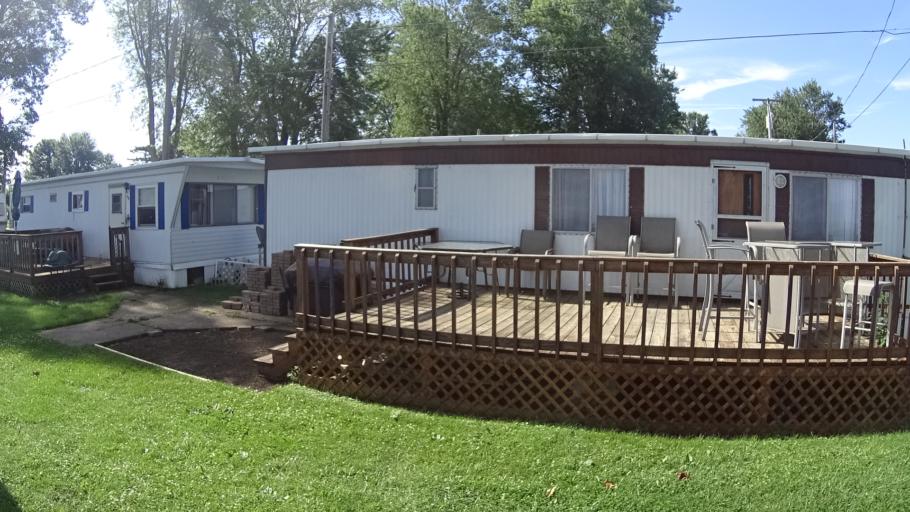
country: US
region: Ohio
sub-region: Erie County
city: Huron
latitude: 41.3804
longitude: -82.4876
